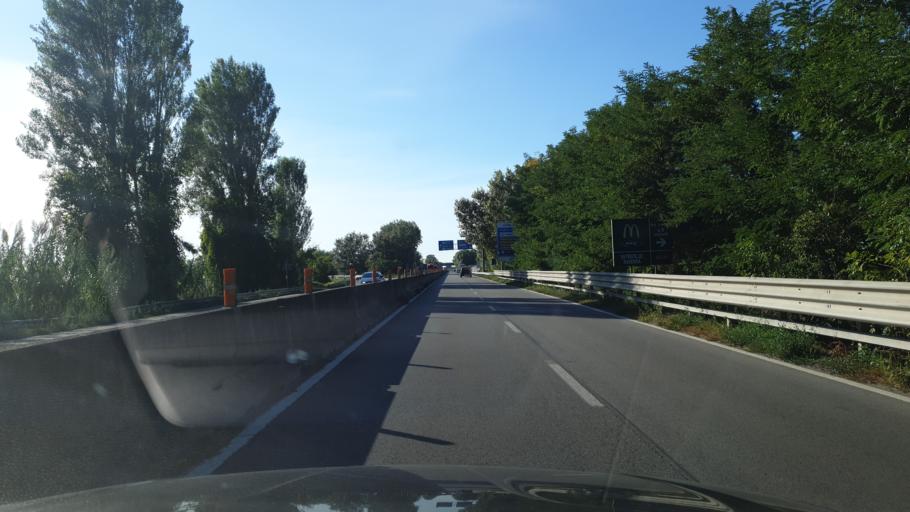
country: IT
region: Emilia-Romagna
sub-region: Provincia di Ravenna
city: Classe
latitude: 44.3698
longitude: 12.2430
